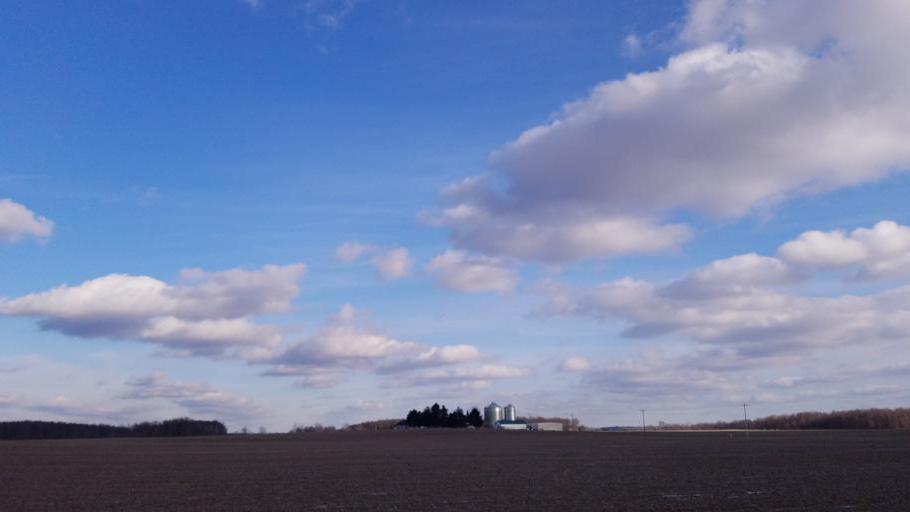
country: US
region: Ohio
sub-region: Morrow County
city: Mount Gilead
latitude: 40.6031
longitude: -82.7287
